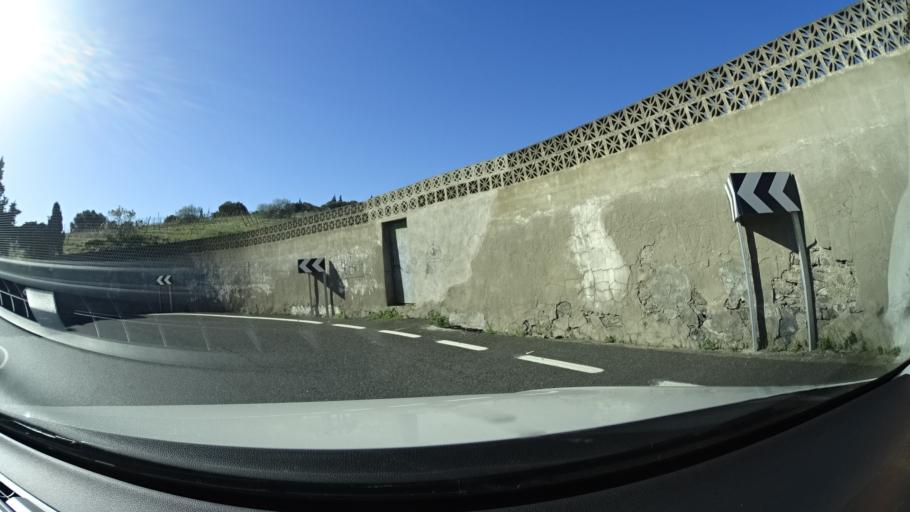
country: ES
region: Canary Islands
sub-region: Provincia de Las Palmas
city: Telde
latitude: 28.0188
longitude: -15.4577
